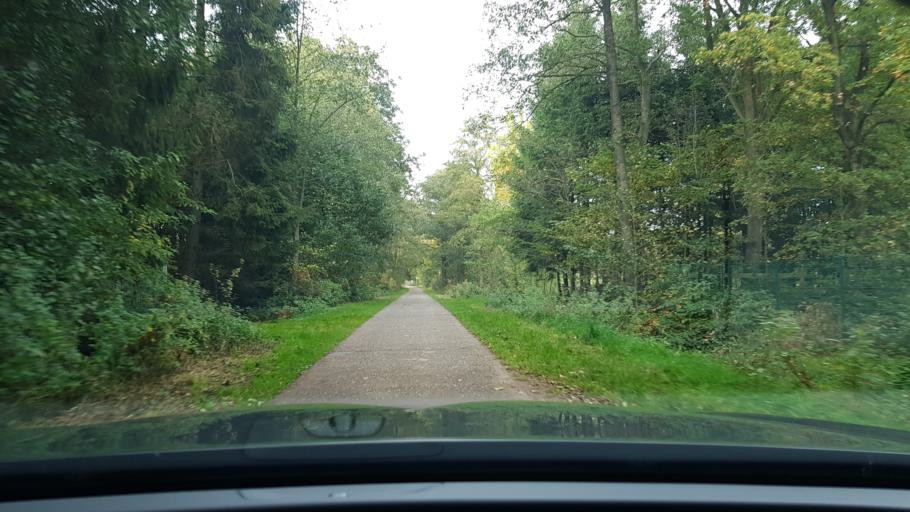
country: DE
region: Lower Saxony
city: Beverstedt
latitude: 53.4200
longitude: 8.8118
